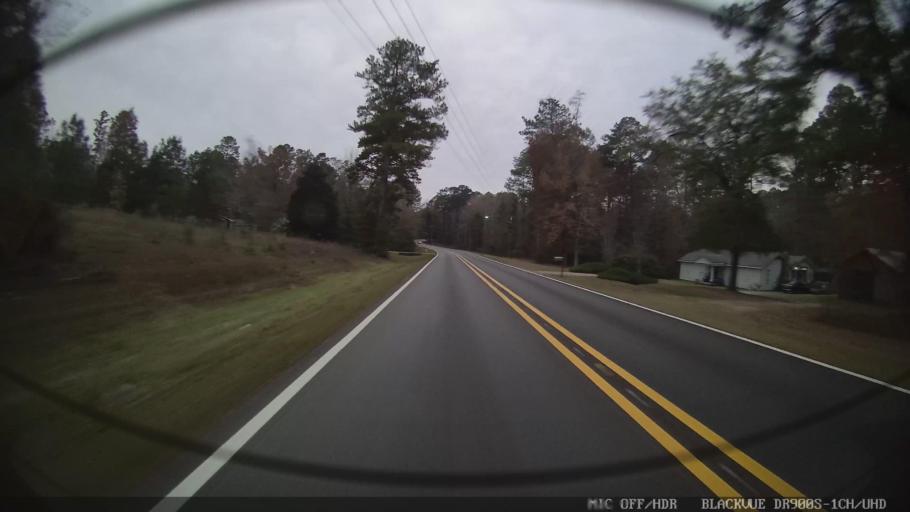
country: US
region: Mississippi
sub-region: Clarke County
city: Quitman
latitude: 32.0436
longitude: -88.7031
